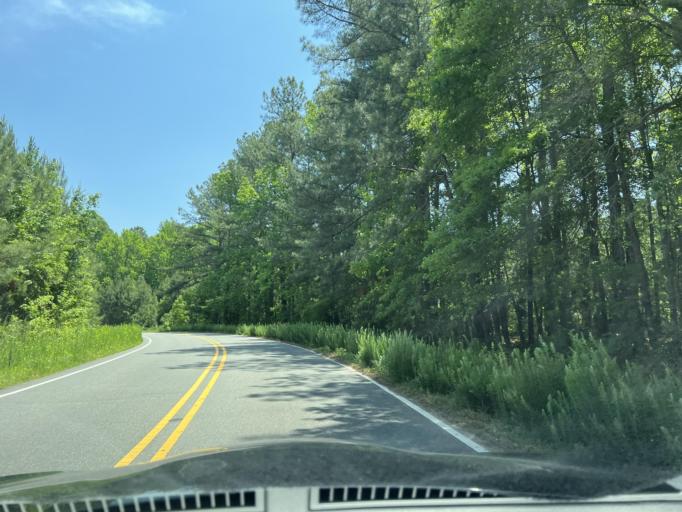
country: US
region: North Carolina
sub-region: Wake County
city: Morrisville
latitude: 35.8516
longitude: -78.8373
